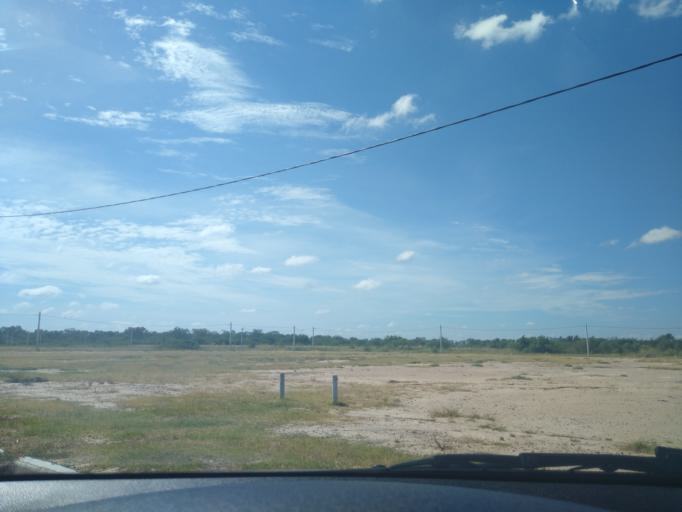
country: AR
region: Chaco
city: Resistencia
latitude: -27.4160
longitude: -58.9599
